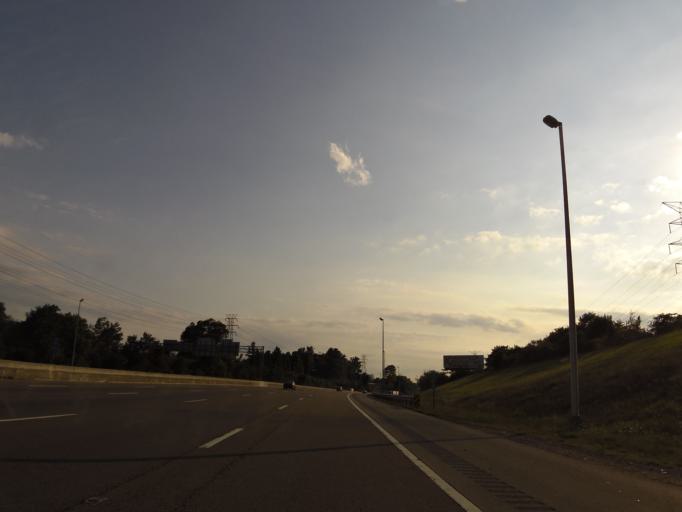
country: US
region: Tennessee
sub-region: Knox County
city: Knoxville
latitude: 35.9608
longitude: -83.9567
